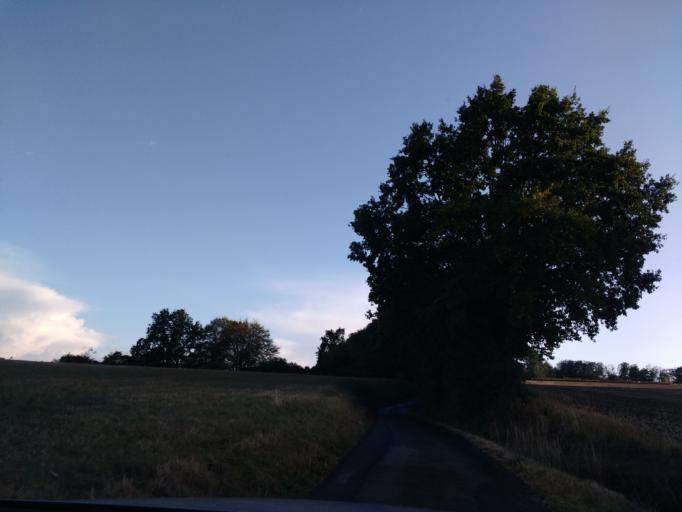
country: DE
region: North Rhine-Westphalia
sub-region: Regierungsbezirk Detmold
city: Detmold
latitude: 51.9643
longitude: 8.9180
